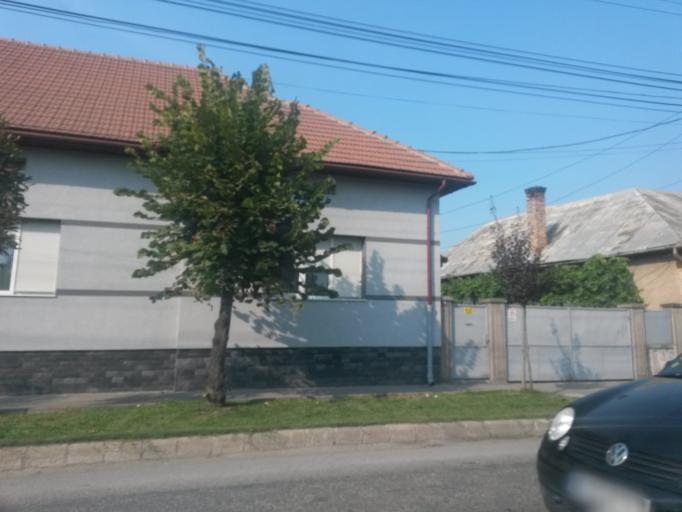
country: RO
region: Cluj
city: Turda
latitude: 46.5800
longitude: 23.7688
